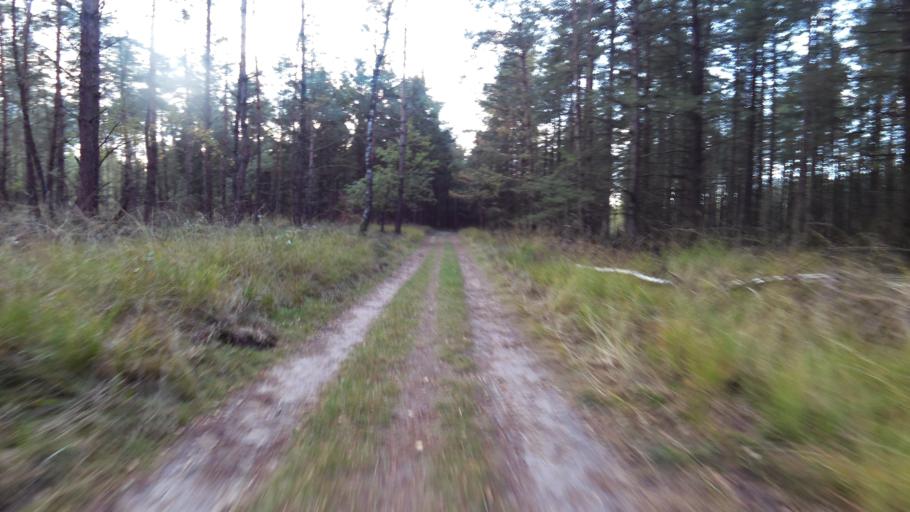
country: NL
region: Gelderland
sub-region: Gemeente Apeldoorn
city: Uddel
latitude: 52.2793
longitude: 5.8189
